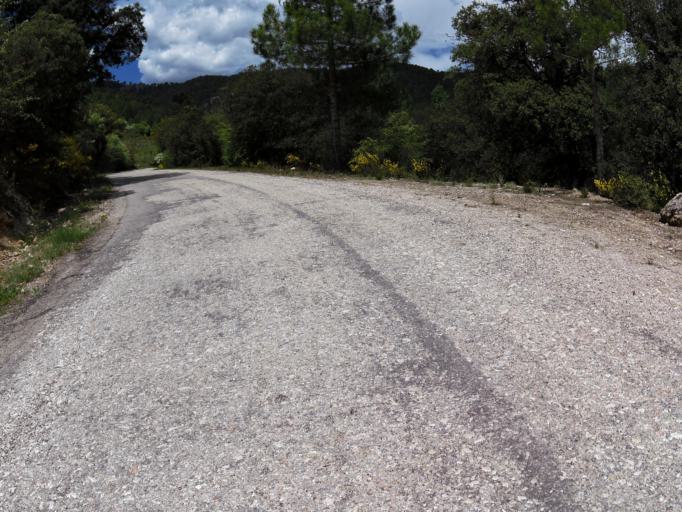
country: ES
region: Castille-La Mancha
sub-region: Provincia de Albacete
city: Paterna del Madera
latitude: 38.5778
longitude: -2.3391
